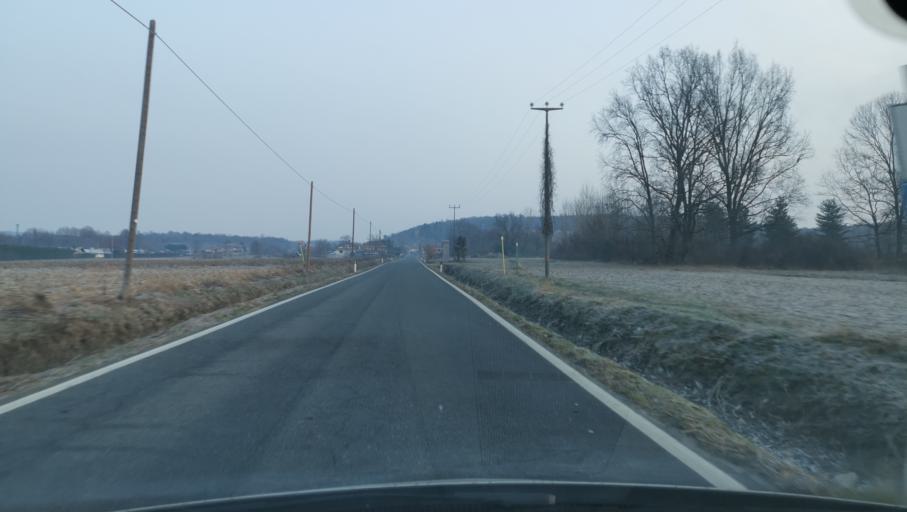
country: IT
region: Piedmont
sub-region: Provincia di Torino
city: Montalenghe
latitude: 45.3268
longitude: 7.8327
